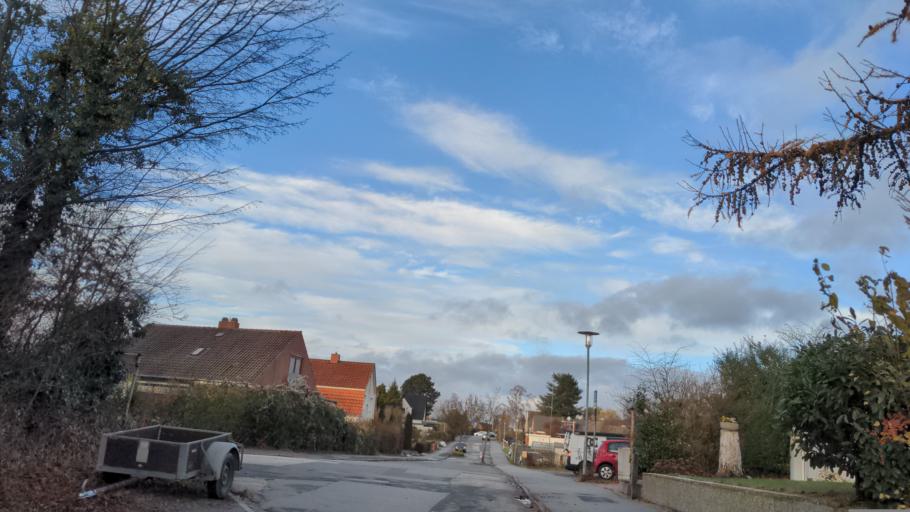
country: DE
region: Schleswig-Holstein
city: Neustadt in Holstein
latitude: 54.1017
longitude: 10.8306
